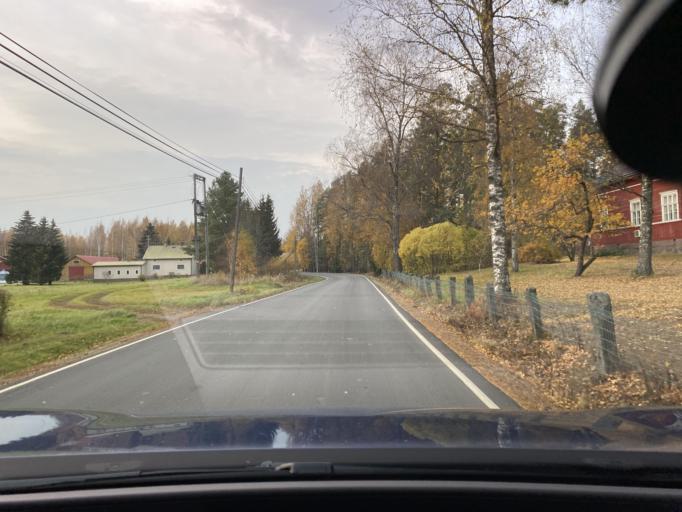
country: FI
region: Varsinais-Suomi
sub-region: Loimaa
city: Alastaro
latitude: 61.0873
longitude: 22.9148
